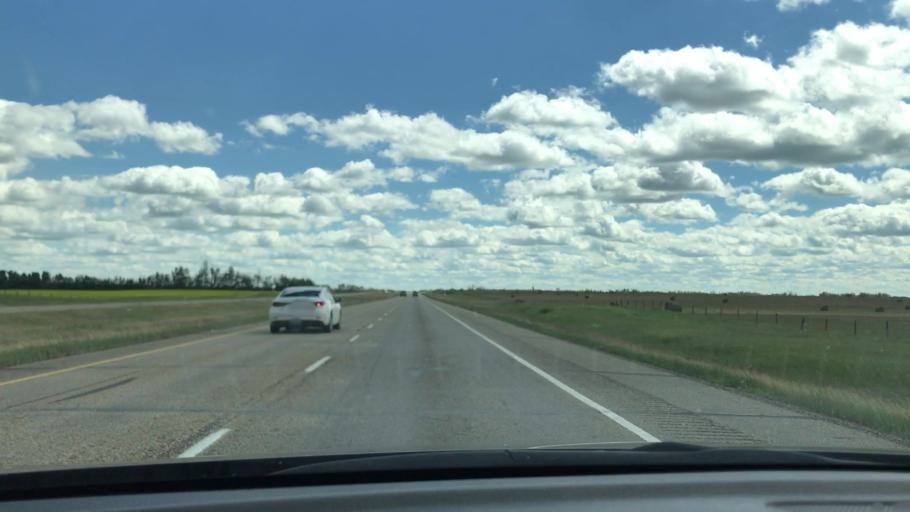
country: CA
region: Alberta
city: Leduc
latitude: 53.1609
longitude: -113.5985
